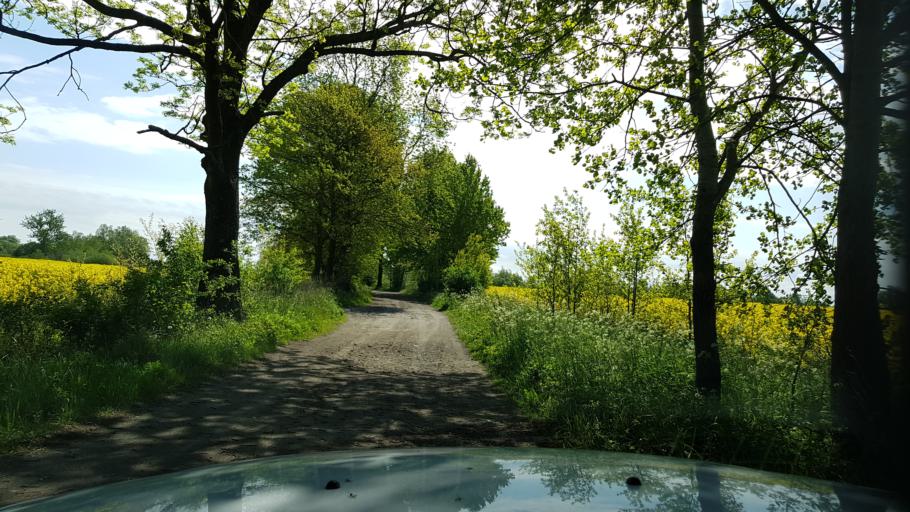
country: PL
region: West Pomeranian Voivodeship
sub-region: Powiat kolobrzeski
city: Ustronie Morskie
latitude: 54.2220
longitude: 15.8210
